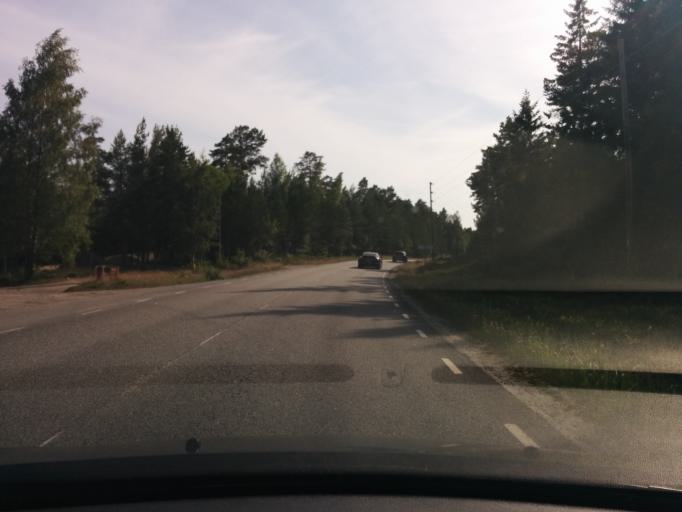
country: SE
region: Stockholm
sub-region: Varmdo Kommun
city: Holo
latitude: 59.3047
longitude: 18.6801
